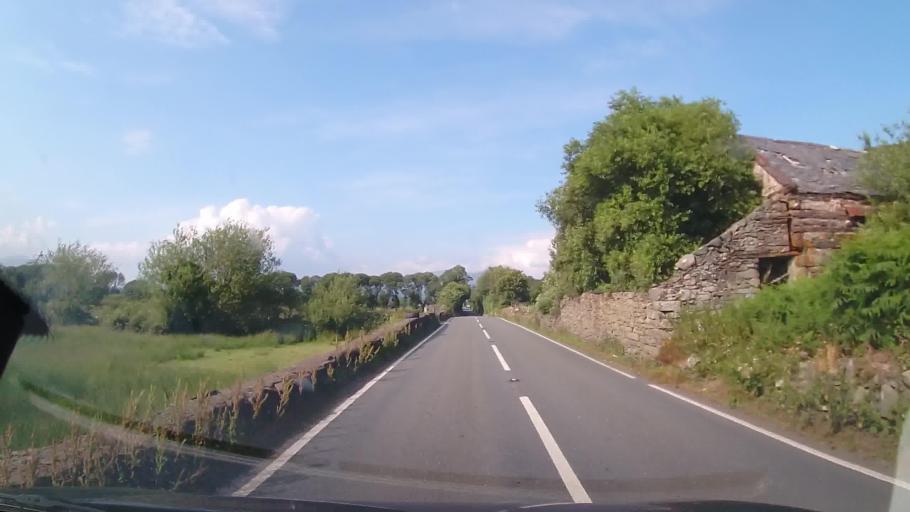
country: GB
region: Wales
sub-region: Gwynedd
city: Penrhyndeudraeth
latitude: 52.8956
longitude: -4.0714
